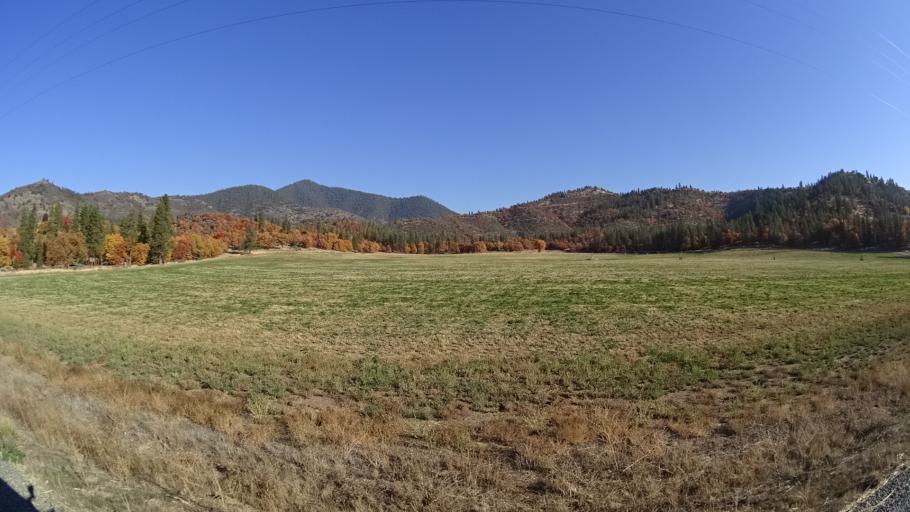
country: US
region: California
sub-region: Siskiyou County
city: Yreka
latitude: 41.6399
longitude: -122.9153
